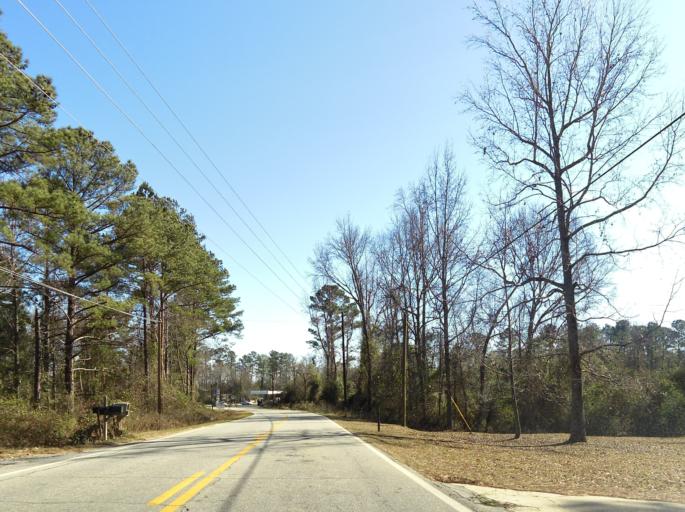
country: US
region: Georgia
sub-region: Bibb County
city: West Point
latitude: 32.8050
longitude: -83.7715
